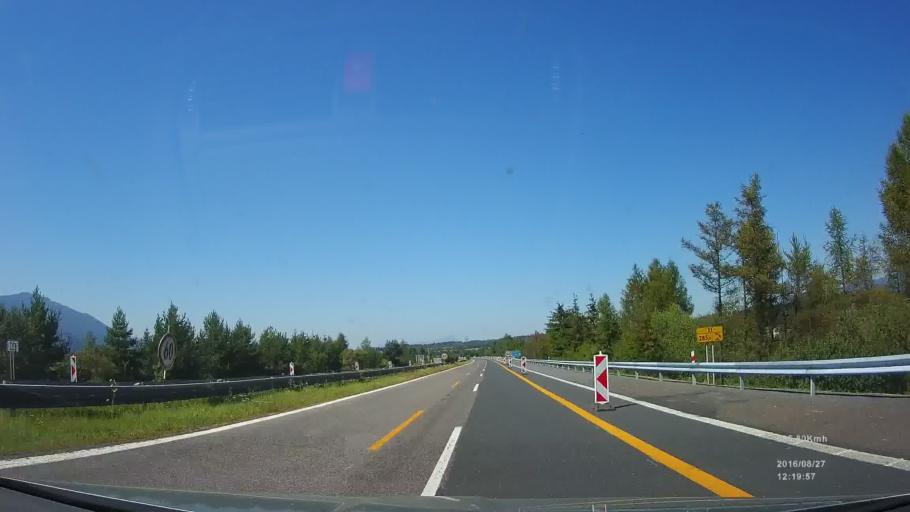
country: SK
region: Zilinsky
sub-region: Okres Zilina
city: Liptovsky Hradok
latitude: 49.0579
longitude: 19.7572
